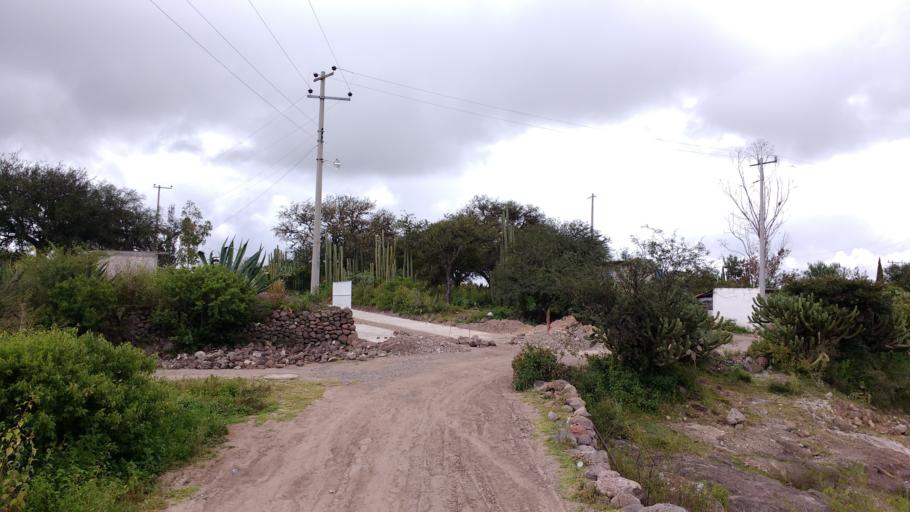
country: MX
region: Hidalgo
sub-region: Tezontepec de Aldama
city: Tenango
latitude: 20.2766
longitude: -99.2875
